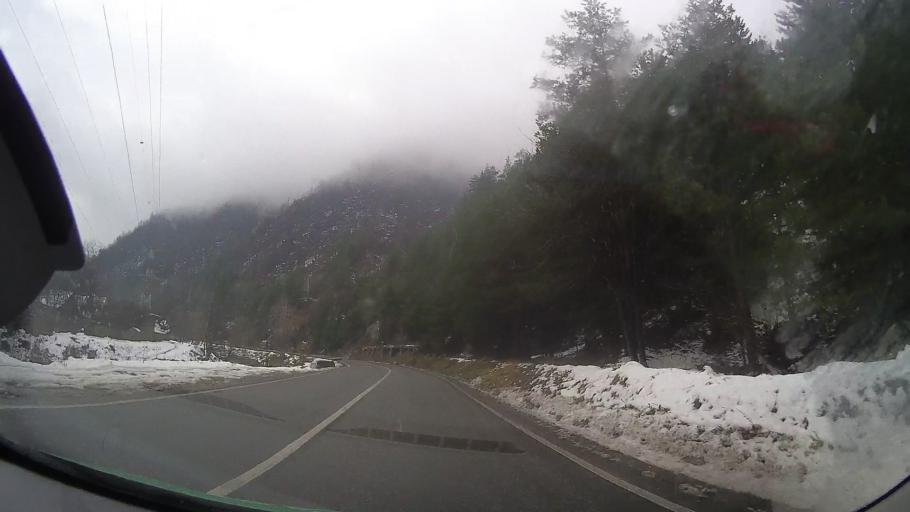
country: RO
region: Neamt
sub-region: Comuna Bicaz
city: Bicaz
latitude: 46.8987
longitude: 26.0590
